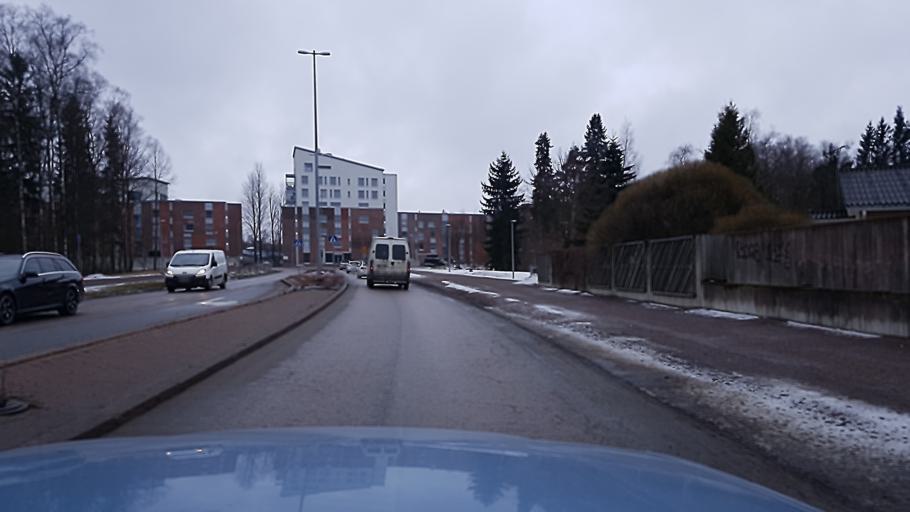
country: FI
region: Uusimaa
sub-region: Helsinki
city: Vantaa
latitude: 60.2798
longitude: 25.0284
